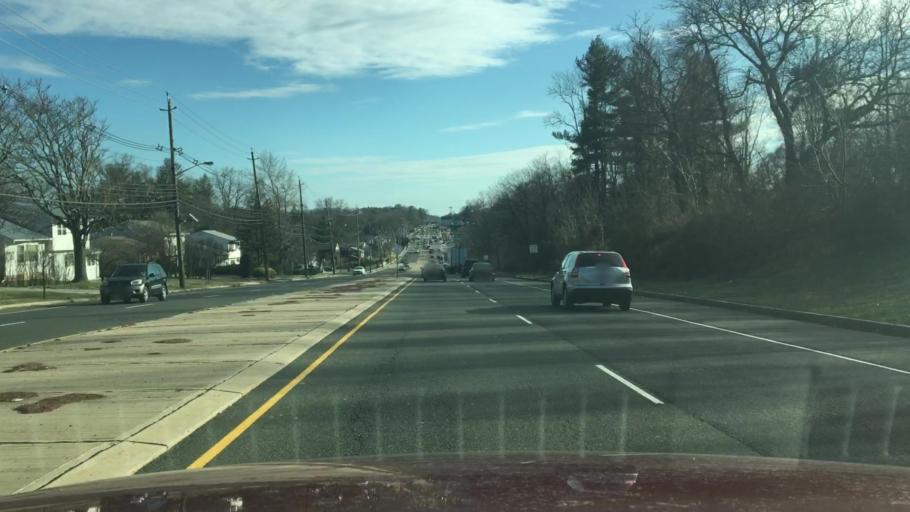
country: US
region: New Jersey
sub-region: Middlesex County
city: Milltown
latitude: 40.4613
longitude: -74.4255
